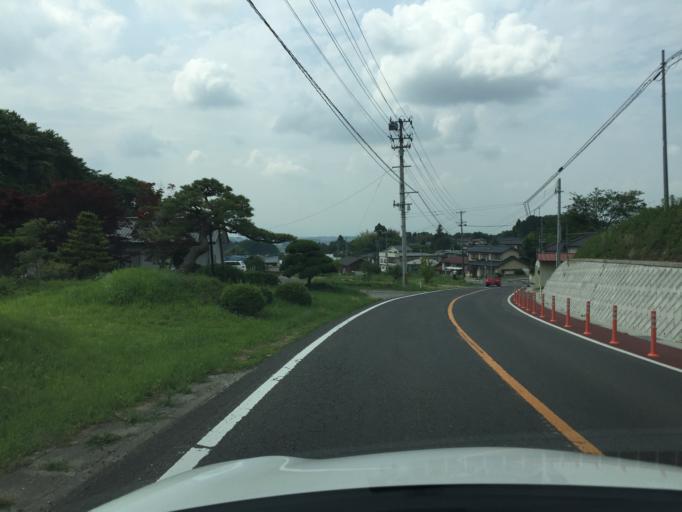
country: JP
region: Fukushima
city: Sukagawa
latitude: 37.2619
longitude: 140.4225
